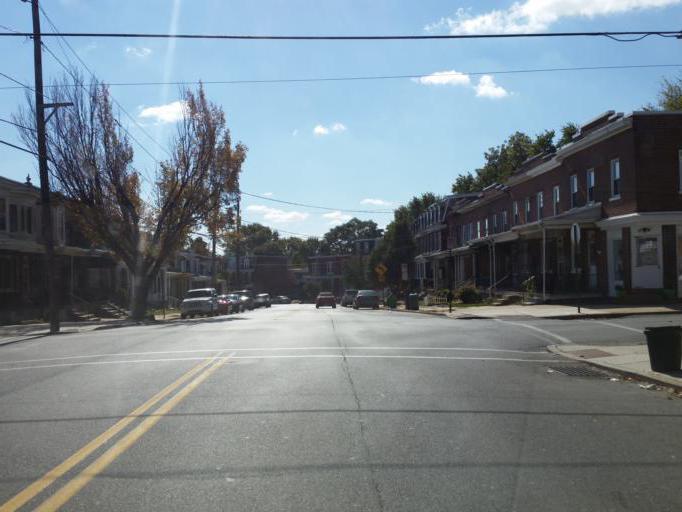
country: US
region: Pennsylvania
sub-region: Lancaster County
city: Lancaster
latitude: 40.0489
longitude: -76.2990
